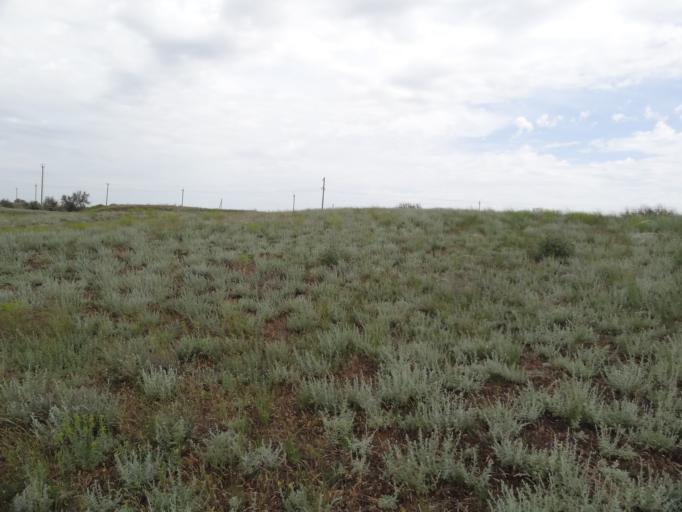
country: RU
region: Saratov
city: Privolzhskiy
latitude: 51.1820
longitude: 45.9216
